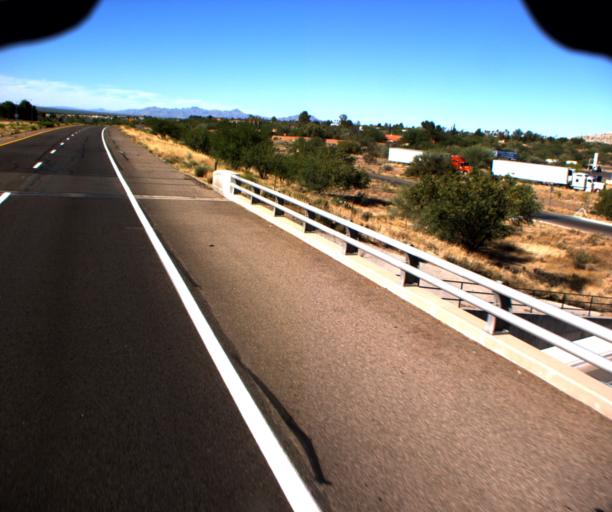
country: US
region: Arizona
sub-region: Pima County
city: Green Valley
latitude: 31.8516
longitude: -110.9938
